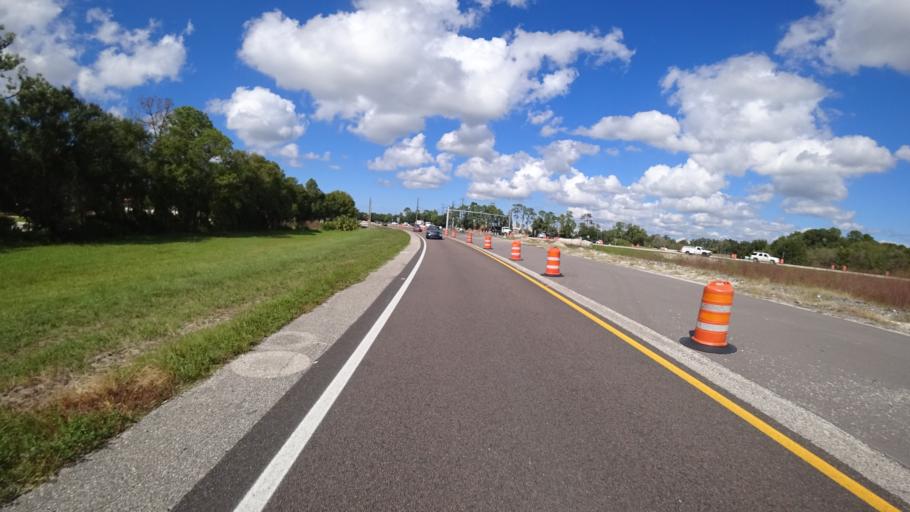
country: US
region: Florida
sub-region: Sarasota County
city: Desoto Lakes
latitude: 27.4410
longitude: -82.4612
